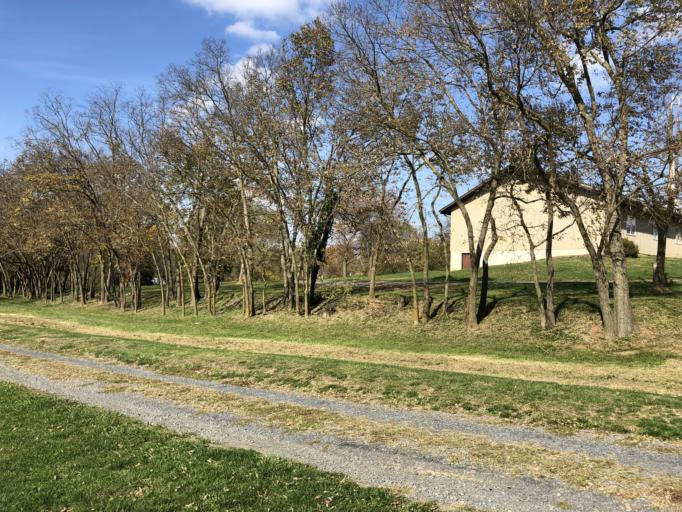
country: US
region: Virginia
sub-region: Frederick County
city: Middletown
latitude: 39.0308
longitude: -78.2802
